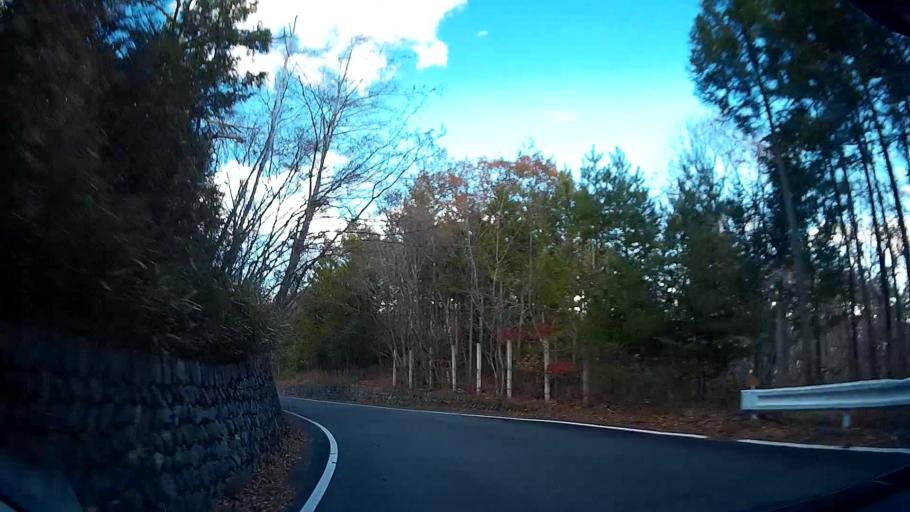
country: JP
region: Yamanashi
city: Otsuki
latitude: 35.7447
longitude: 138.9515
